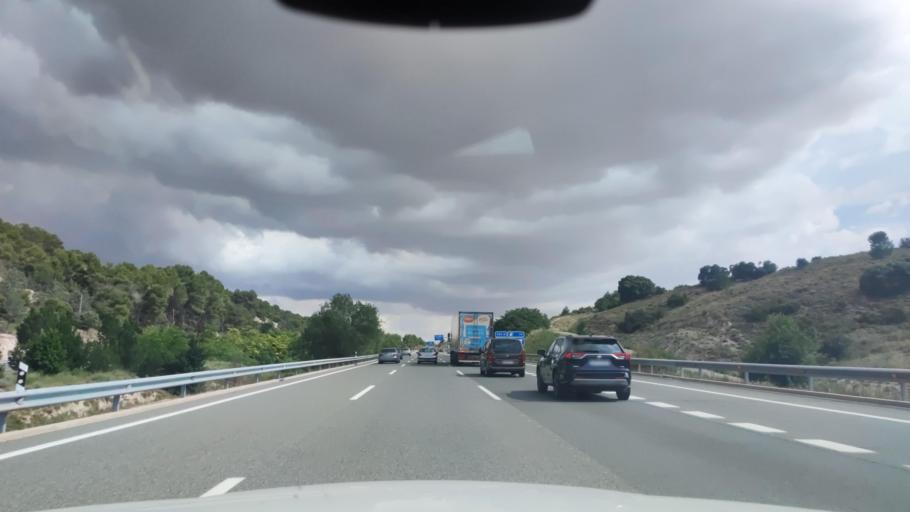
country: ES
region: Castille-La Mancha
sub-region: Provincia de Cuenca
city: Belinchon
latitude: 40.0247
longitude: -3.0359
